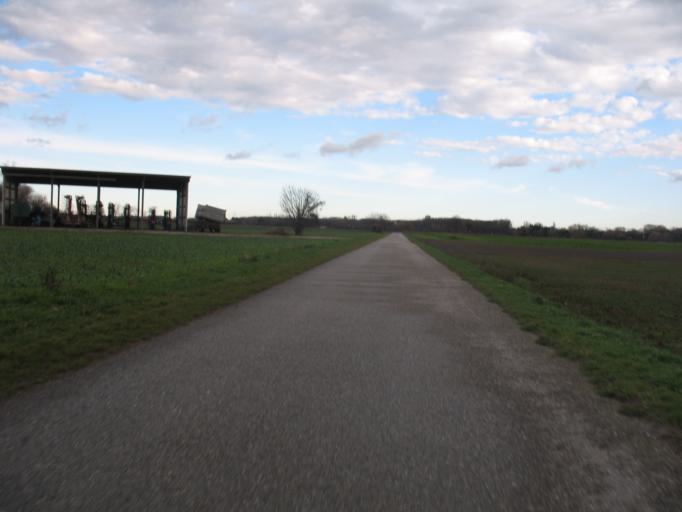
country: AT
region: Lower Austria
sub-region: Politischer Bezirk Wien-Umgebung
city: Himberg
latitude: 48.0668
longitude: 16.4222
